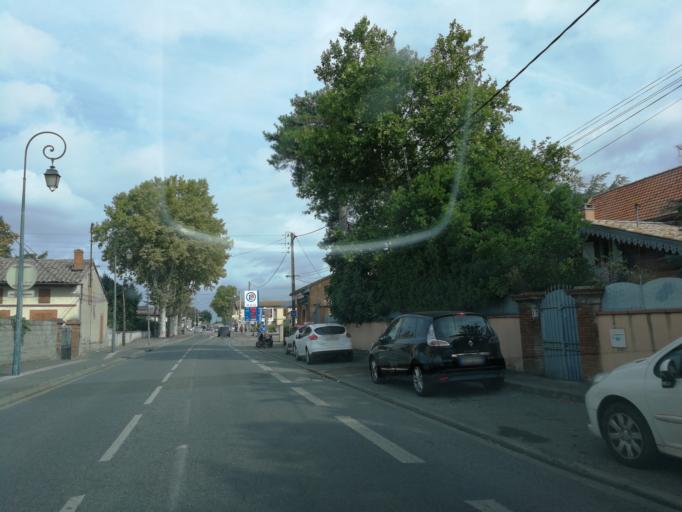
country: FR
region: Midi-Pyrenees
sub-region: Departement de la Haute-Garonne
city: Aucamville
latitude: 43.6773
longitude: 1.4237
